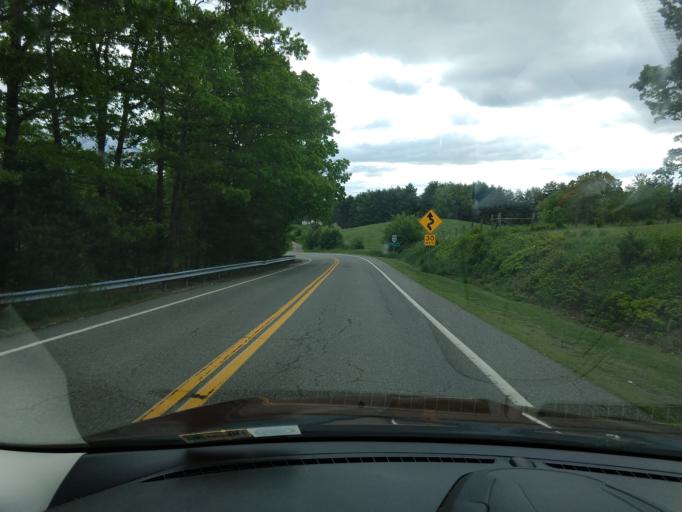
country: US
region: Virginia
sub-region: City of Galax
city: Galax
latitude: 36.7795
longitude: -80.9868
